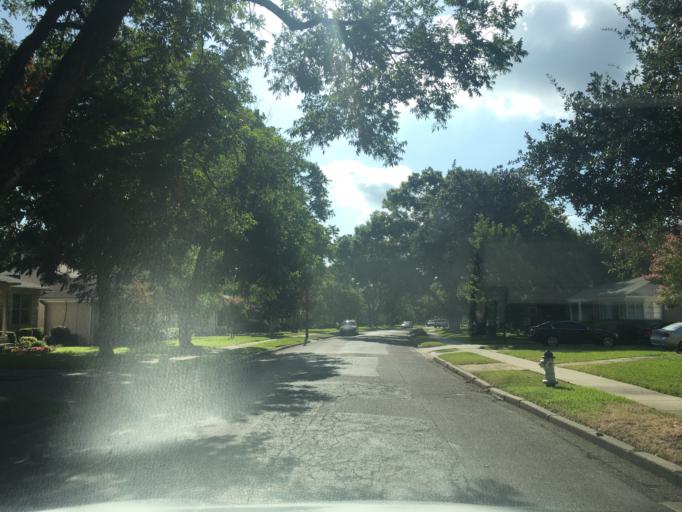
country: US
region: Texas
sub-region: Dallas County
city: Highland Park
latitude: 32.8349
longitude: -96.7596
